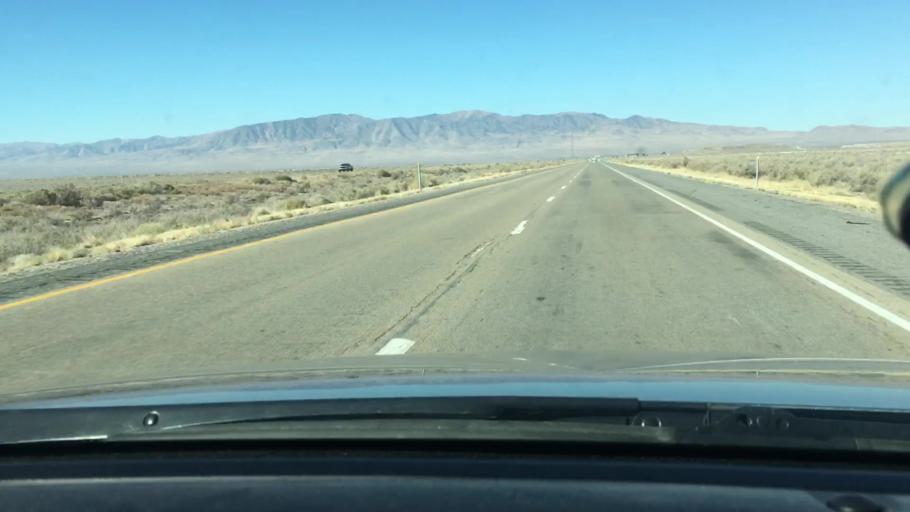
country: US
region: Utah
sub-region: Tooele County
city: Grantsville
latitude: 40.7550
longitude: -112.7419
